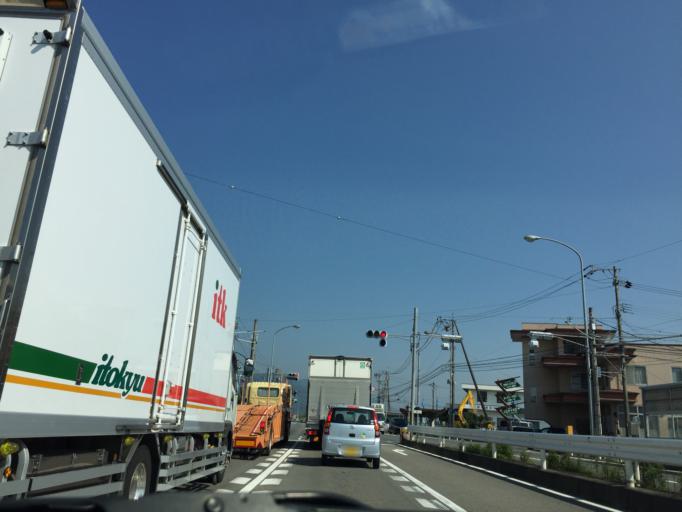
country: JP
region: Aichi
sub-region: Tsushima-shi
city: Tsushima
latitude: 35.0996
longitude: 136.6664
